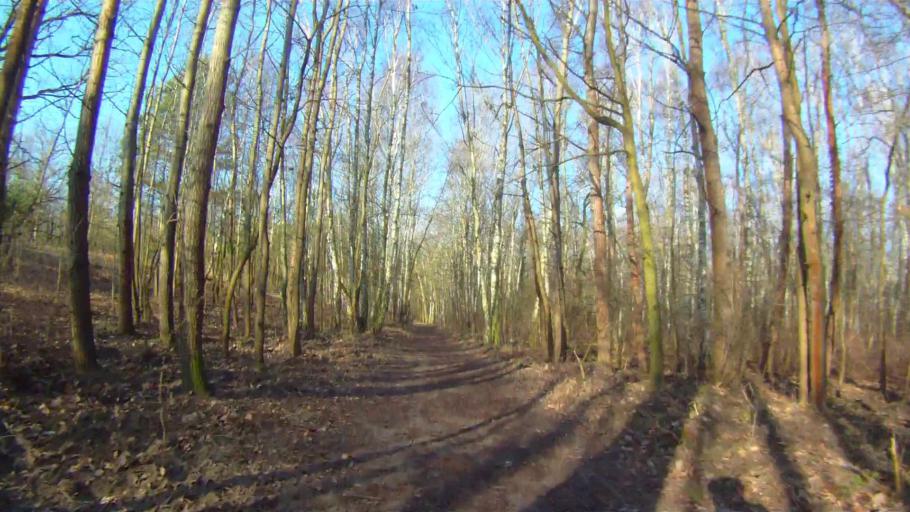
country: DE
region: Brandenburg
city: Woltersdorf
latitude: 52.4622
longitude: 13.7370
